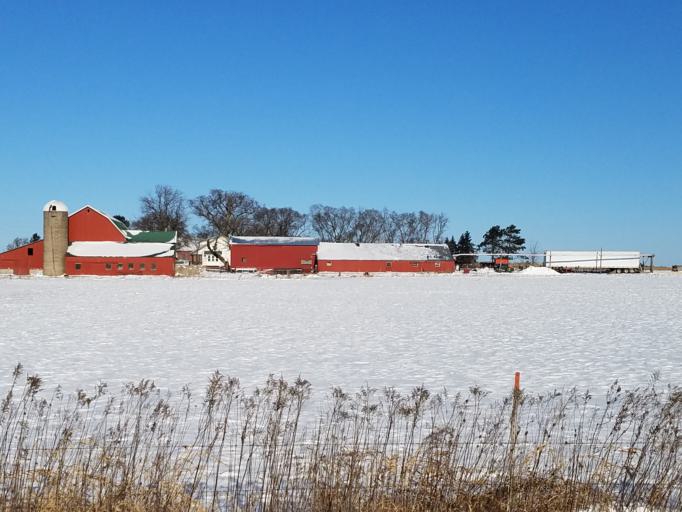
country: US
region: Wisconsin
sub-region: Clark County
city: Neillsville
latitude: 44.5534
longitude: -90.3953
